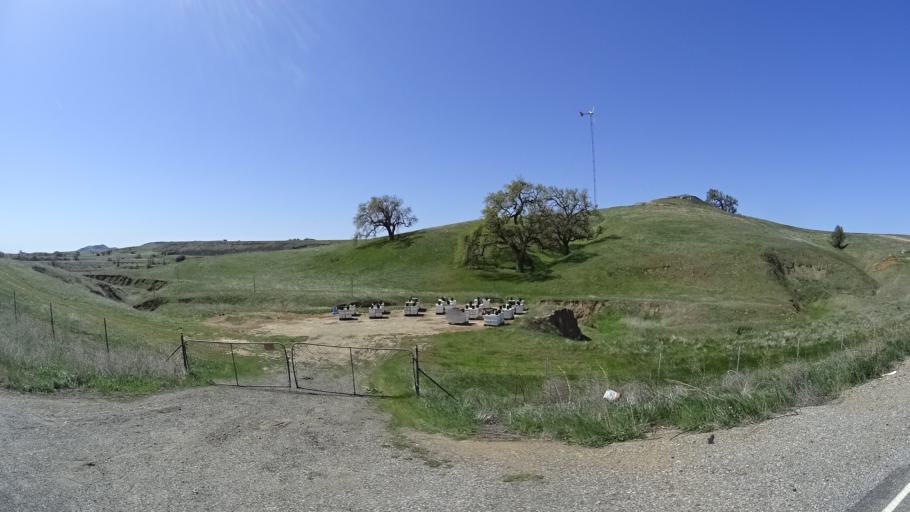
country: US
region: California
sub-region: Glenn County
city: Orland
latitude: 39.8250
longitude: -122.3337
